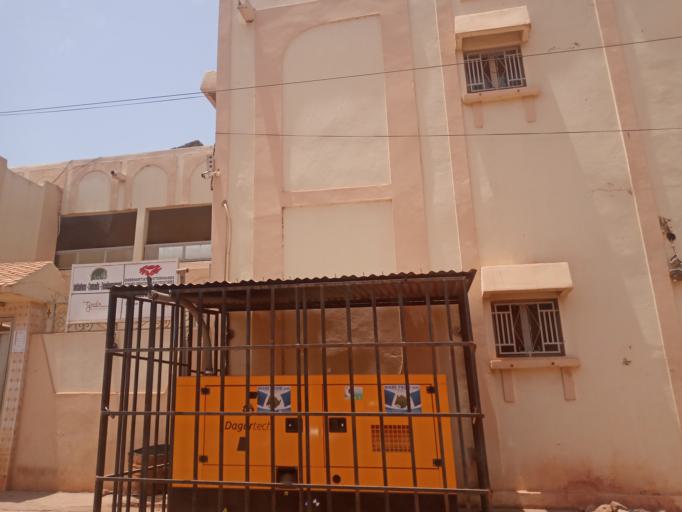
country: ML
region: Bamako
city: Bamako
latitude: 12.6176
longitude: -7.9982
